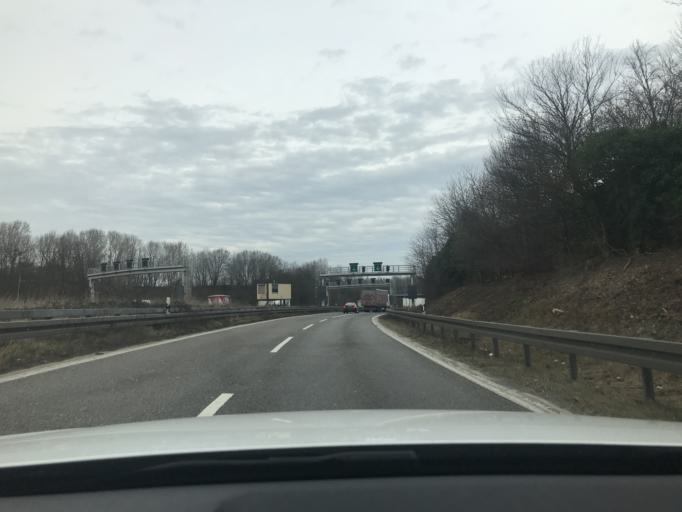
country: DE
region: North Rhine-Westphalia
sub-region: Regierungsbezirk Koln
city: Frechen
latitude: 50.9267
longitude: 6.8476
